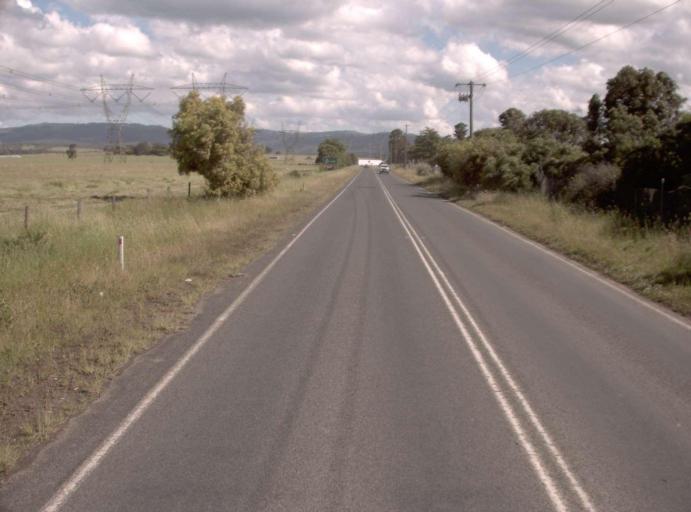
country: AU
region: Victoria
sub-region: Latrobe
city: Morwell
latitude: -38.2591
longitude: 146.4342
